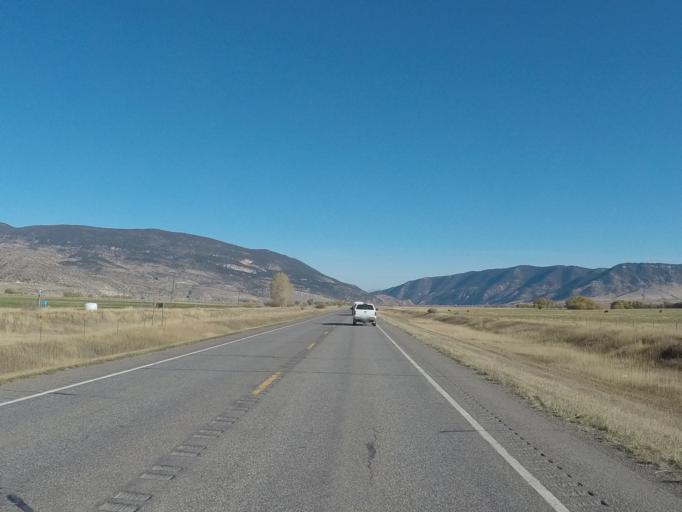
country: US
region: Montana
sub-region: Park County
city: Livingston
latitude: 45.5296
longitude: -110.6057
